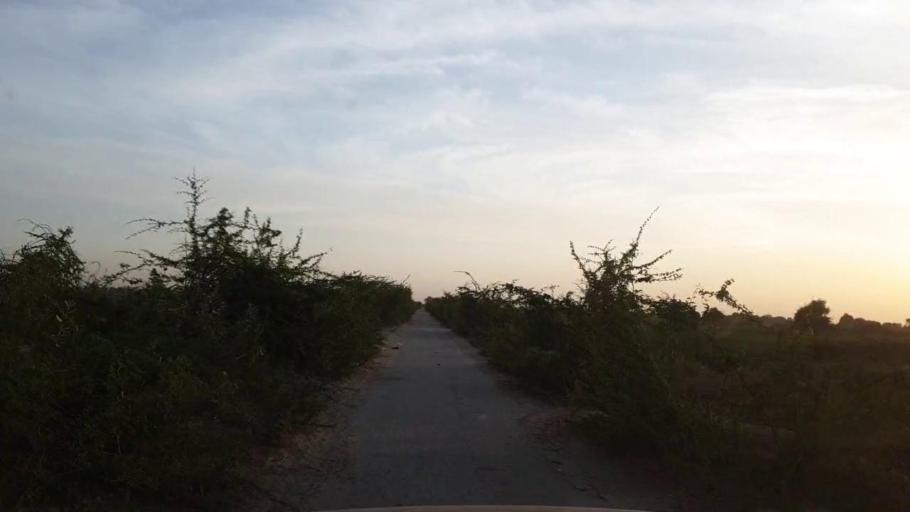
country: PK
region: Sindh
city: Kunri
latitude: 25.1160
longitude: 69.5649
